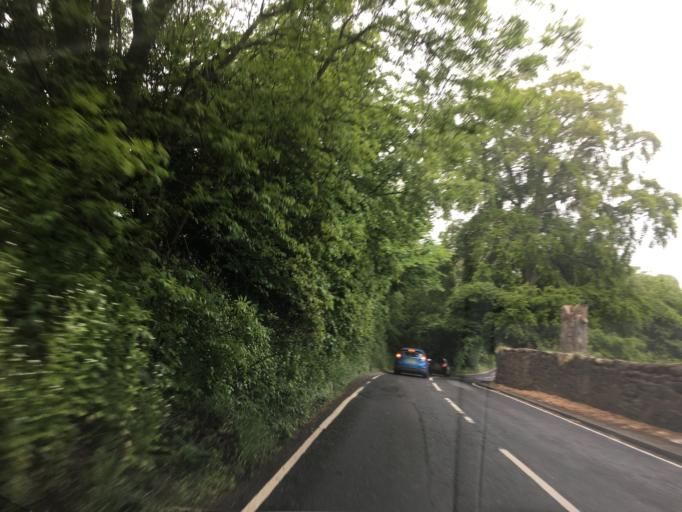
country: GB
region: Scotland
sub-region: Midlothian
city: Penicuik
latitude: 55.8396
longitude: -3.1992
